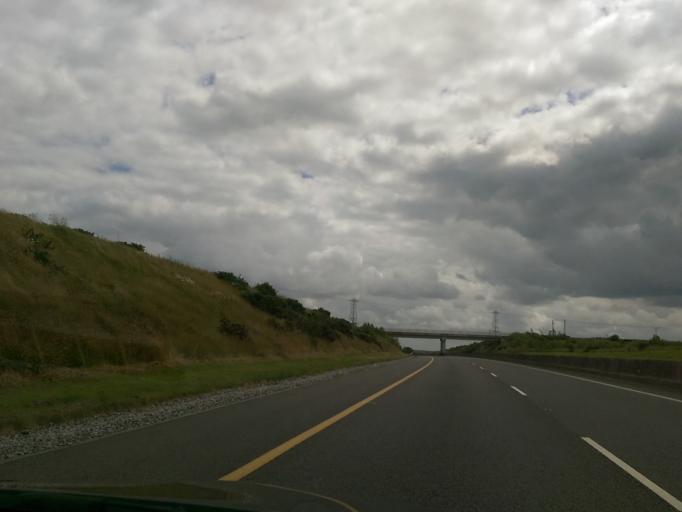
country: IE
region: Munster
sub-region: County Cork
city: Mitchelstown
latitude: 52.2190
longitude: -8.2849
